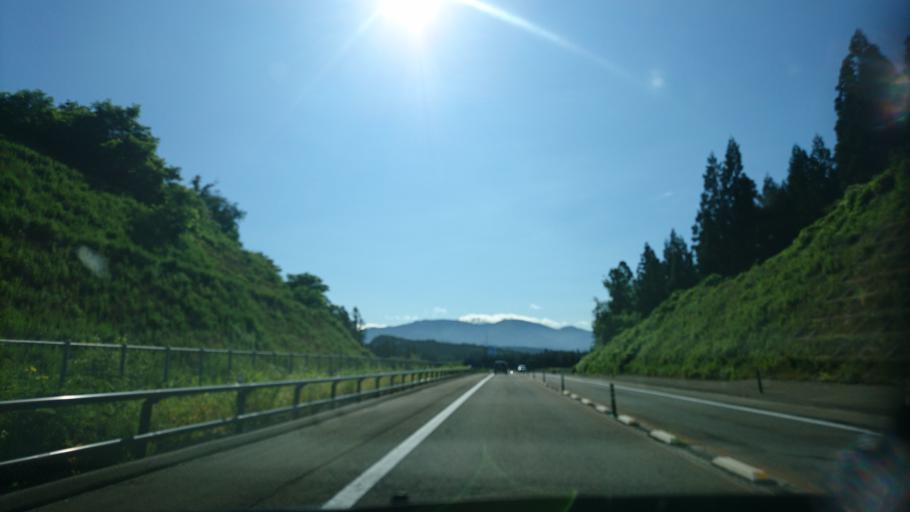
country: JP
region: Akita
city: Kakunodatemachi
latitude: 39.5952
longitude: 140.5334
